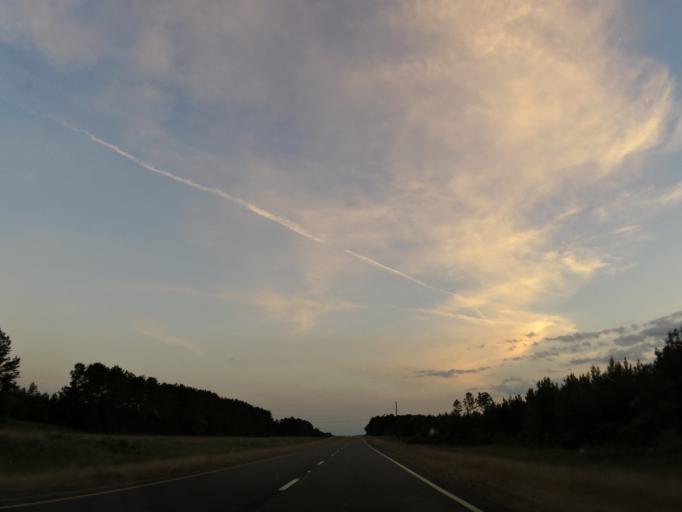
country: US
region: Mississippi
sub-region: Kemper County
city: De Kalb
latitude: 32.7179
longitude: -88.4794
